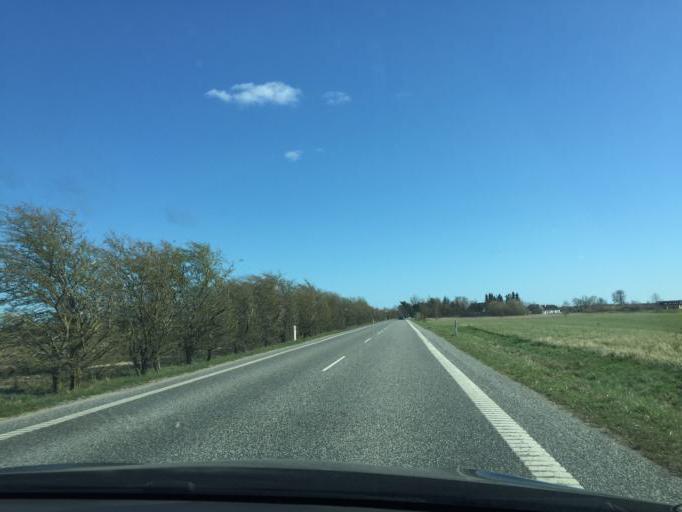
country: DK
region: South Denmark
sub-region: Kerteminde Kommune
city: Langeskov
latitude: 55.3301
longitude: 10.5367
